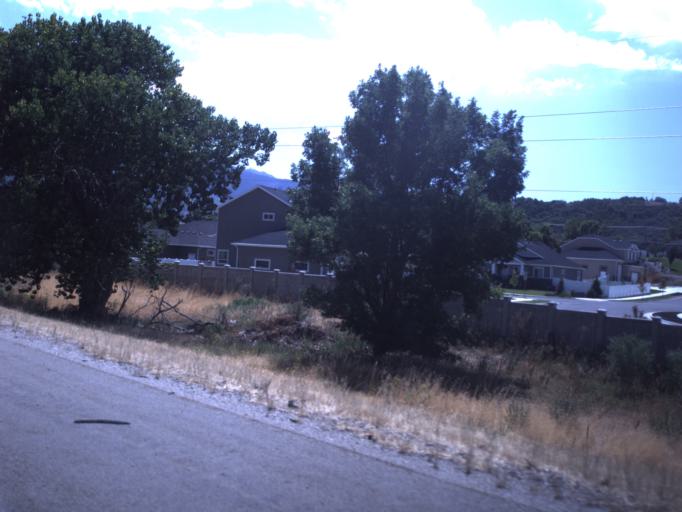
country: US
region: Utah
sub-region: Davis County
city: South Weber
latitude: 41.1371
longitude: -111.9497
